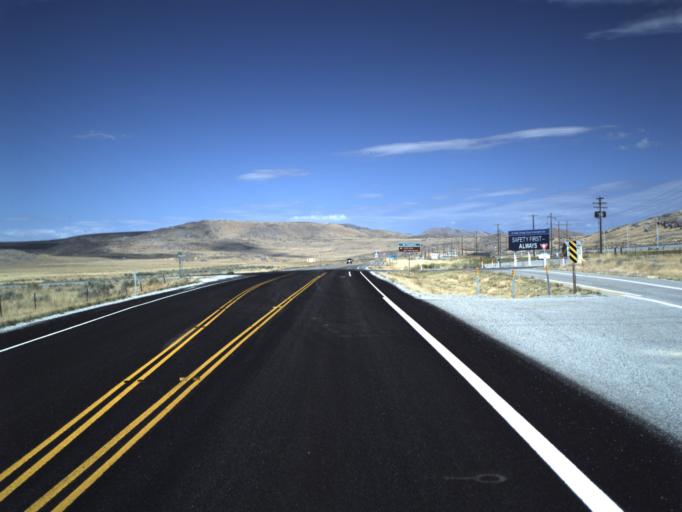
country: US
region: Utah
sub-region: Box Elder County
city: Tremonton
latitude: 41.6356
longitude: -112.4229
